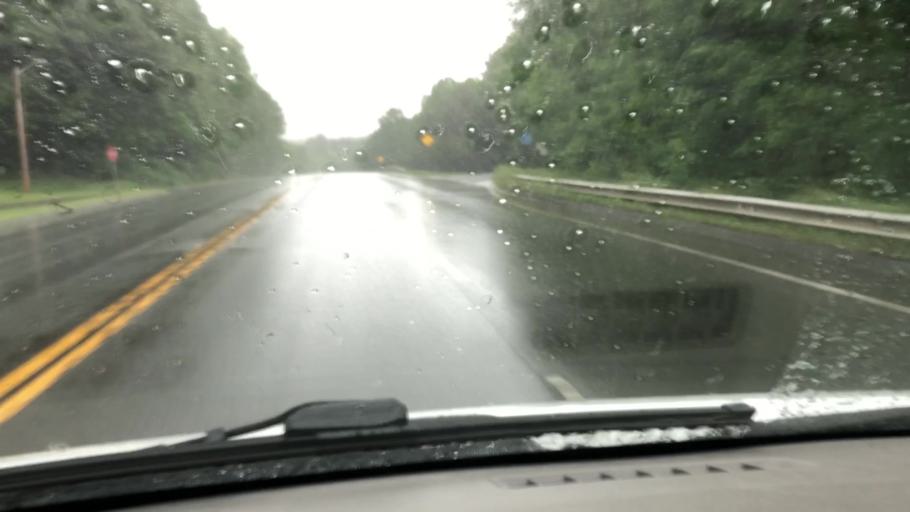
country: US
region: Massachusetts
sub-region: Berkshire County
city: Adams
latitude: 42.5878
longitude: -73.1466
